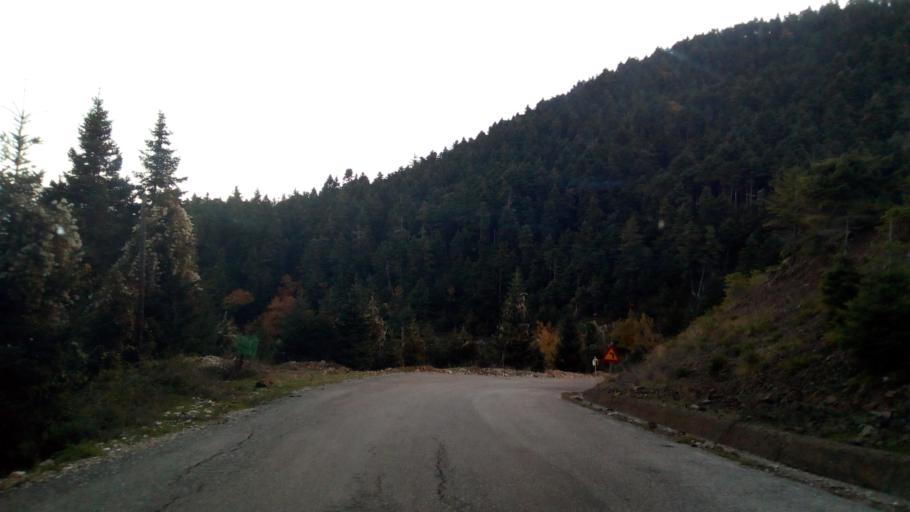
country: GR
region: West Greece
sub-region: Nomos Aitolias kai Akarnanias
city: Thermo
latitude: 38.6342
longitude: 21.8345
